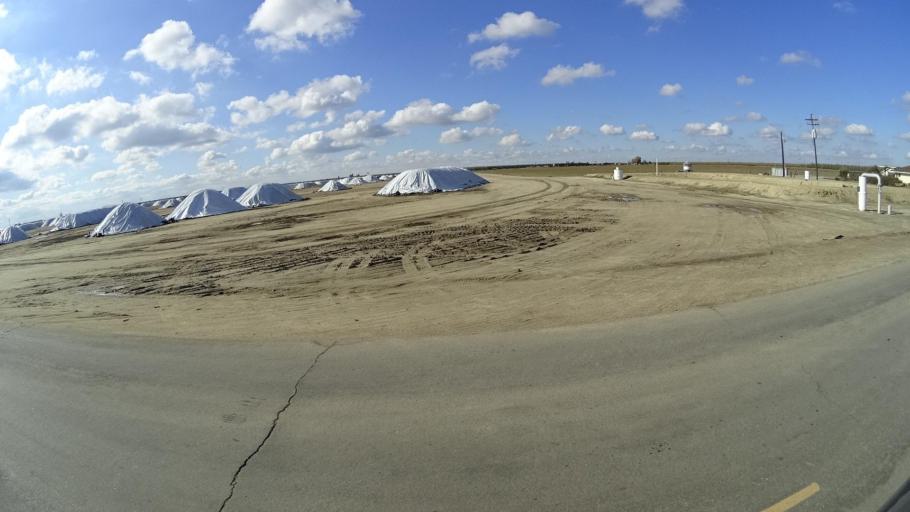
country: US
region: California
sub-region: Kern County
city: McFarland
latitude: 35.6994
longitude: -119.2408
